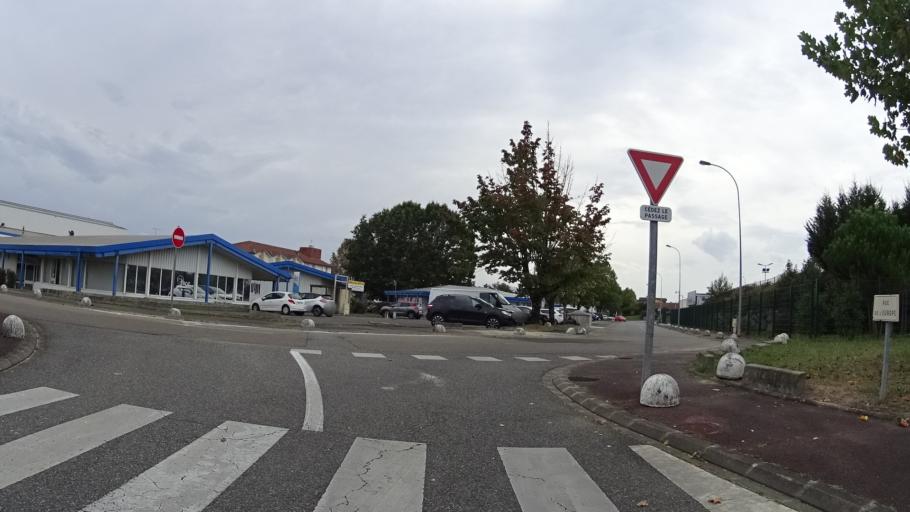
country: FR
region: Aquitaine
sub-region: Departement des Landes
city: Saint-Paul-les-Dax
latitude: 43.7280
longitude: -1.0778
